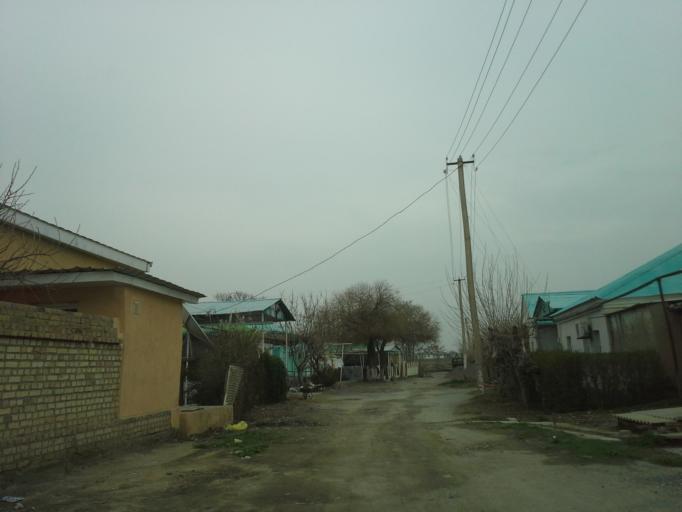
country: TM
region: Ahal
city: Abadan
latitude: 37.9675
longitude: 58.2213
